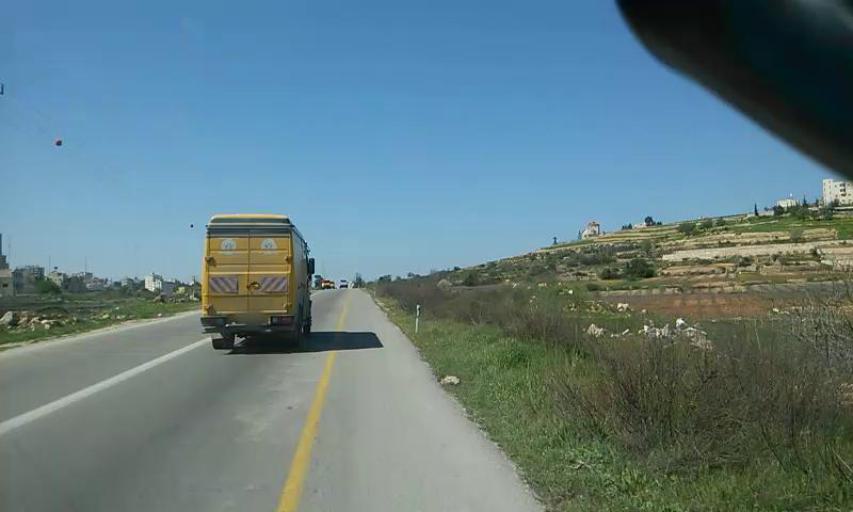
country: PS
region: West Bank
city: Halhul
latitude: 31.5632
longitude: 35.1041
